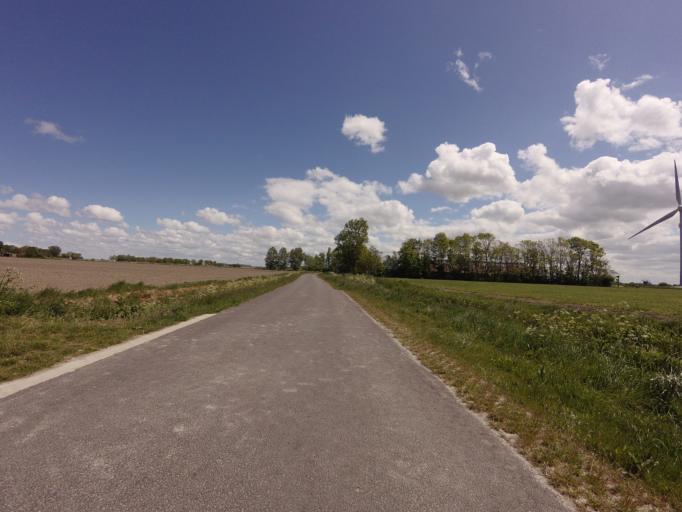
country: NL
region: Friesland
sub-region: Gemeente Harlingen
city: Harlingen
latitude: 53.1372
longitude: 5.4322
